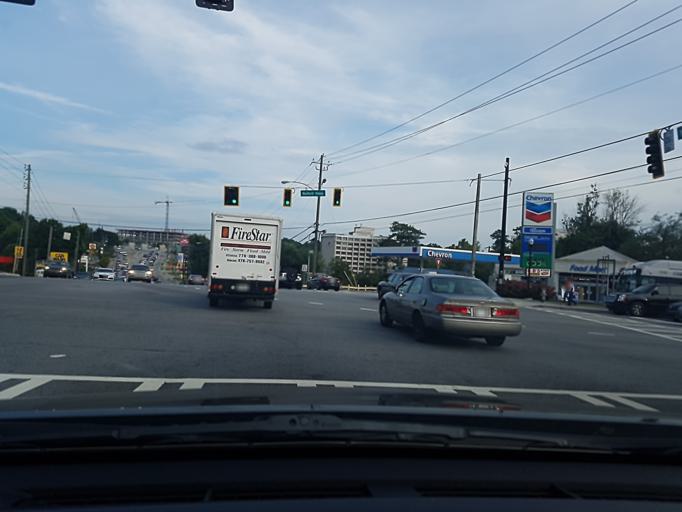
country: US
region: Georgia
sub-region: DeKalb County
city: North Atlanta
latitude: 33.8338
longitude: -84.3405
